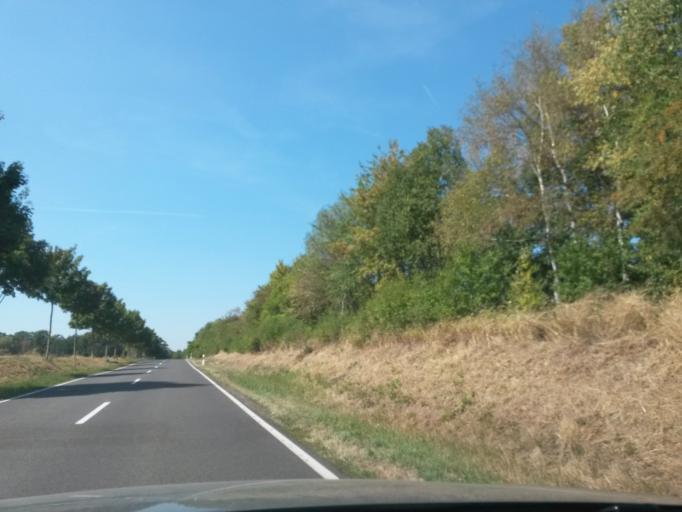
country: DE
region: Brandenburg
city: Belzig
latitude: 52.1580
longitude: 12.5191
